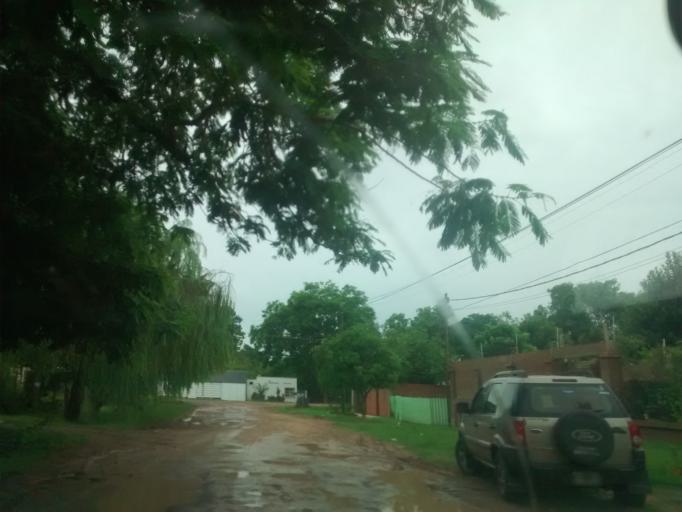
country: AR
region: Chaco
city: Resistencia
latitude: -27.4385
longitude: -58.9795
